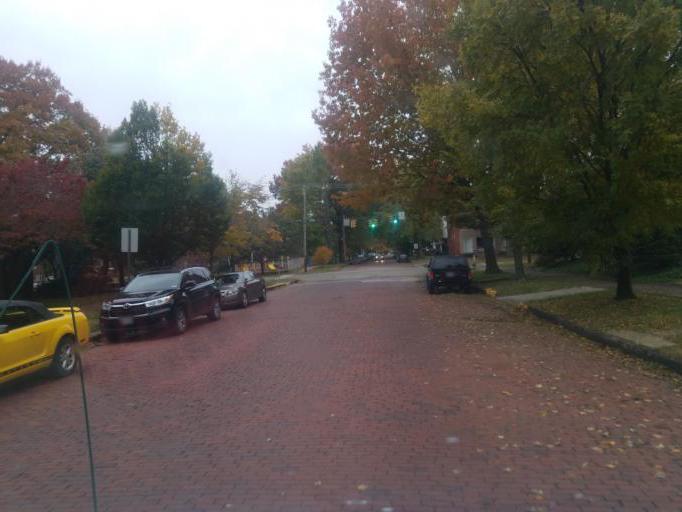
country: US
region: Ohio
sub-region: Washington County
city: Marietta
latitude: 39.4233
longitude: -81.4564
